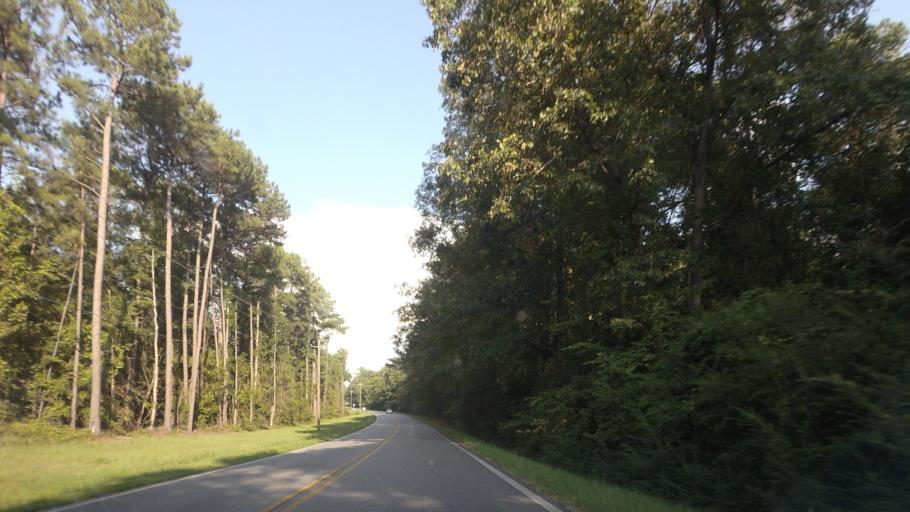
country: US
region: Georgia
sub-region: Bibb County
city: Macon
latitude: 32.8476
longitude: -83.7034
